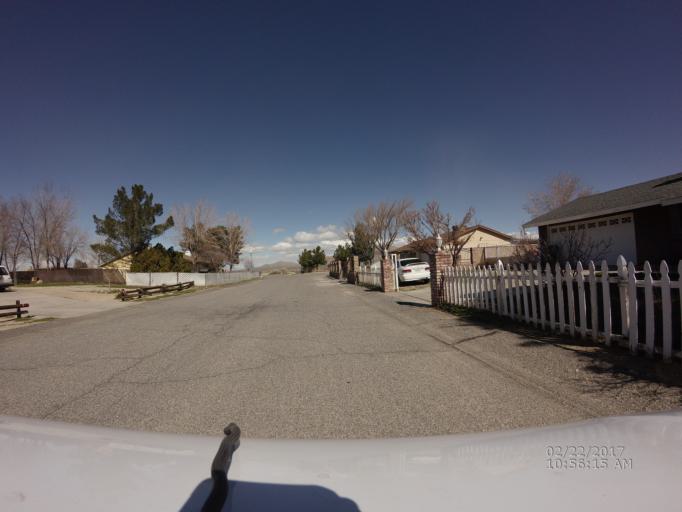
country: US
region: California
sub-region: Los Angeles County
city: Lake Los Angeles
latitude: 34.6297
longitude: -117.8110
